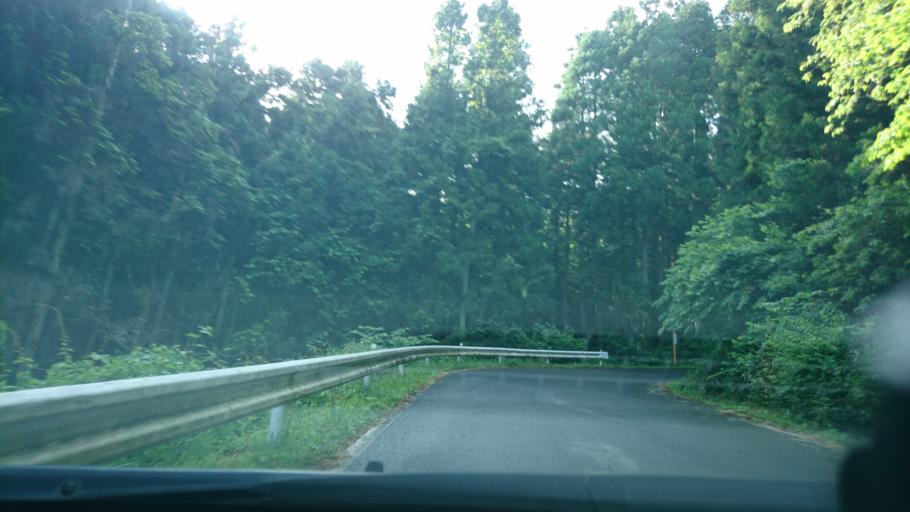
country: JP
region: Iwate
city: Ichinoseki
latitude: 38.8652
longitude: 141.2779
